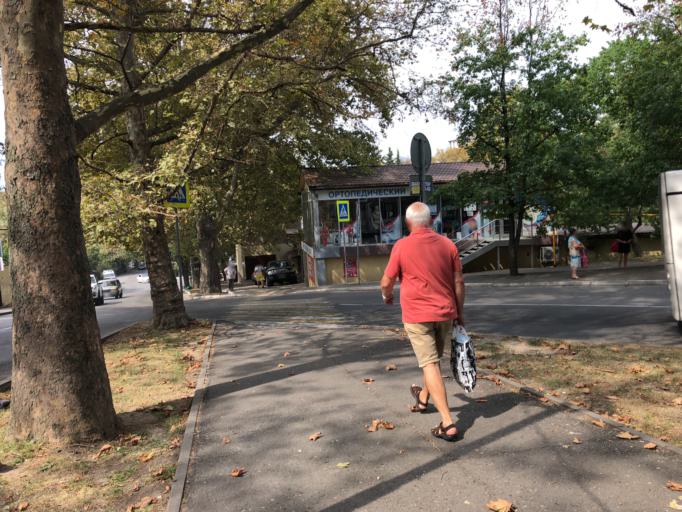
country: RU
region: Krasnodarskiy
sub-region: Sochi City
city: Sochi
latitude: 43.5944
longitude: 39.7359
